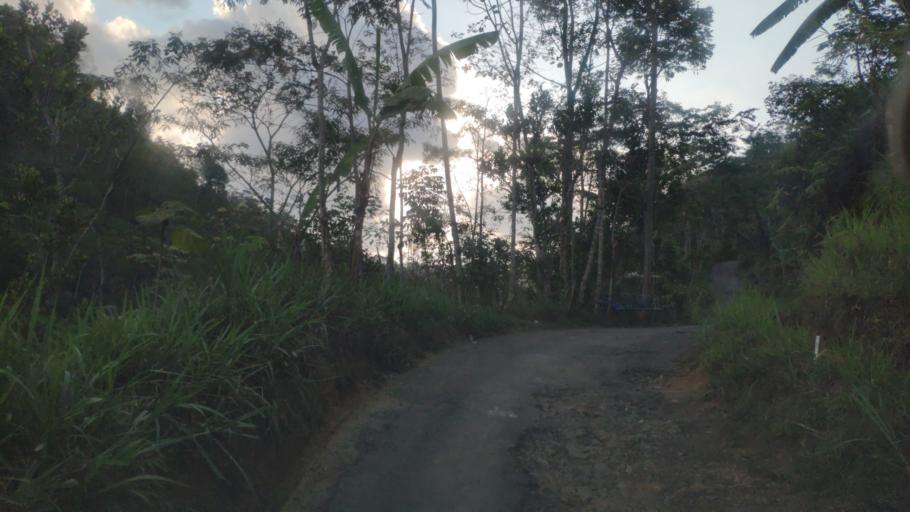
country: ID
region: Central Java
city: Buaran
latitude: -7.2482
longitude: 109.5732
